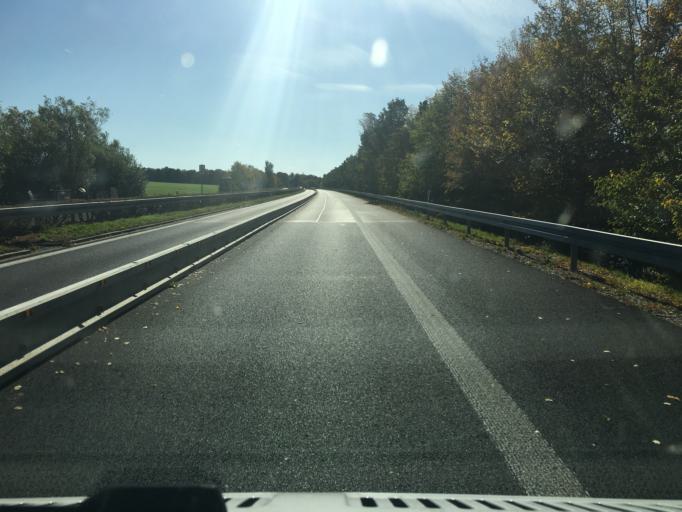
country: DE
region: Saxony
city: Zwickau
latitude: 50.7520
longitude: 12.5018
